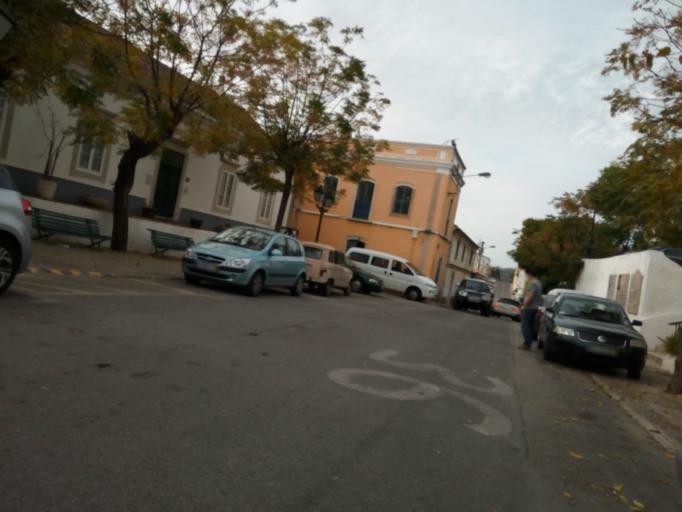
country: PT
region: Faro
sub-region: Faro
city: Santa Barbara de Nexe
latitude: 37.1037
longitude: -7.9637
